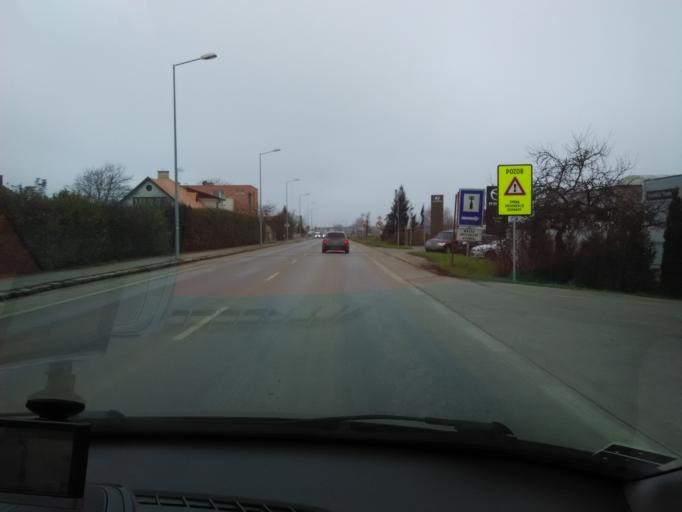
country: SK
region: Trenciansky
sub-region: Okres Trencin
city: Trencin
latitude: 48.8976
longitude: 18.0126
